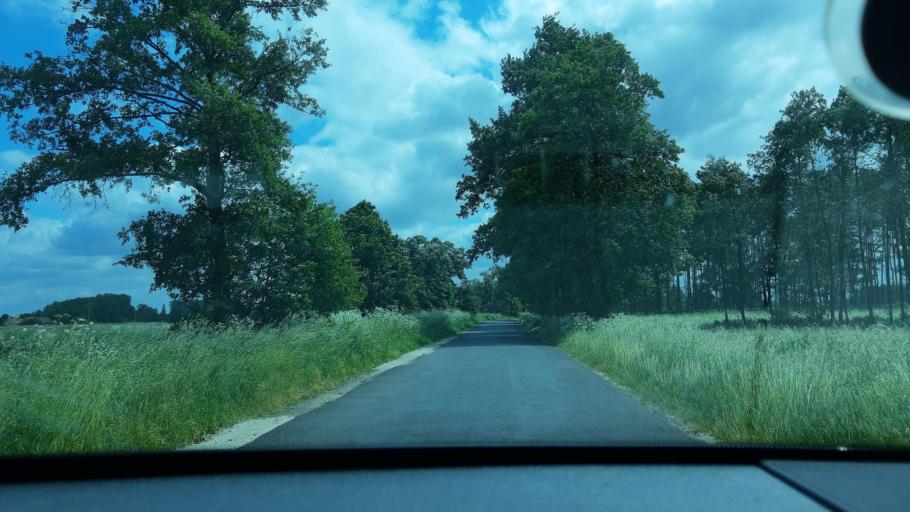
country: PL
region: Lodz Voivodeship
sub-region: Powiat zdunskowolski
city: Zapolice
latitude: 51.5395
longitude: 18.8210
